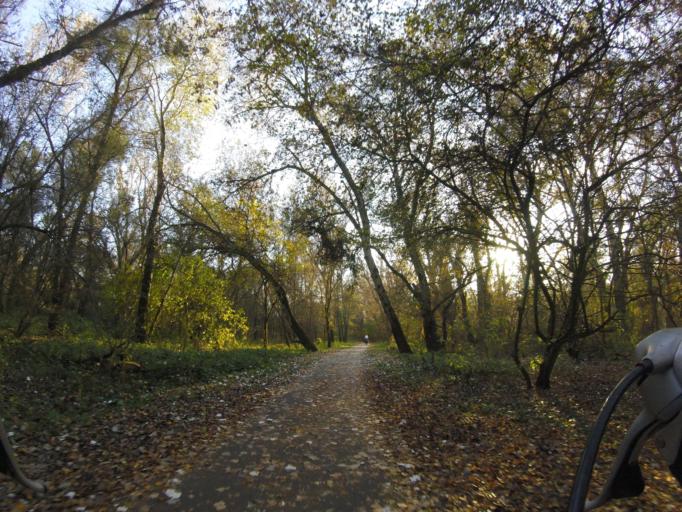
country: HU
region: Pest
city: Vac
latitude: 47.7582
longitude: 19.1373
